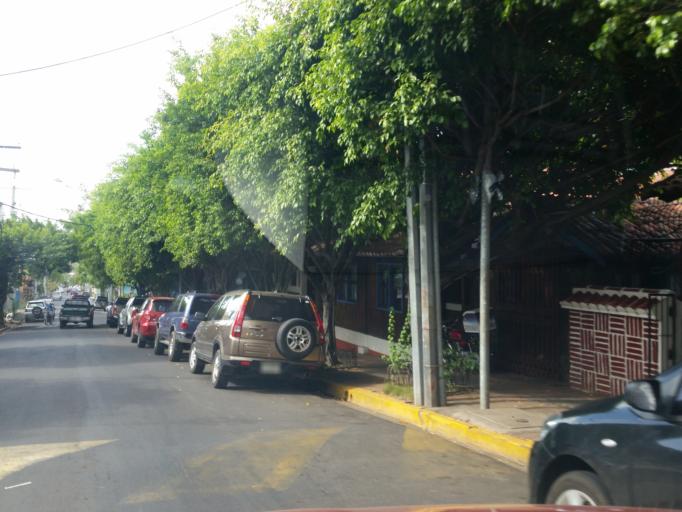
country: NI
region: Managua
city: Managua
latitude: 12.1427
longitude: -86.2761
